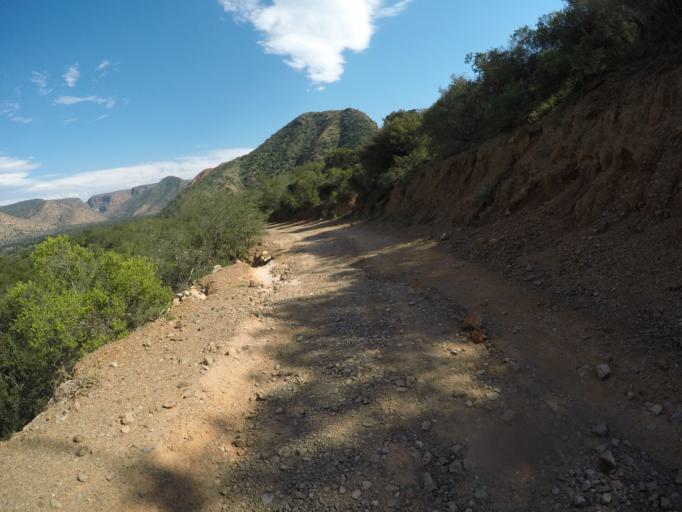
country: ZA
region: Eastern Cape
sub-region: Cacadu District Municipality
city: Kareedouw
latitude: -33.6590
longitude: 24.3997
